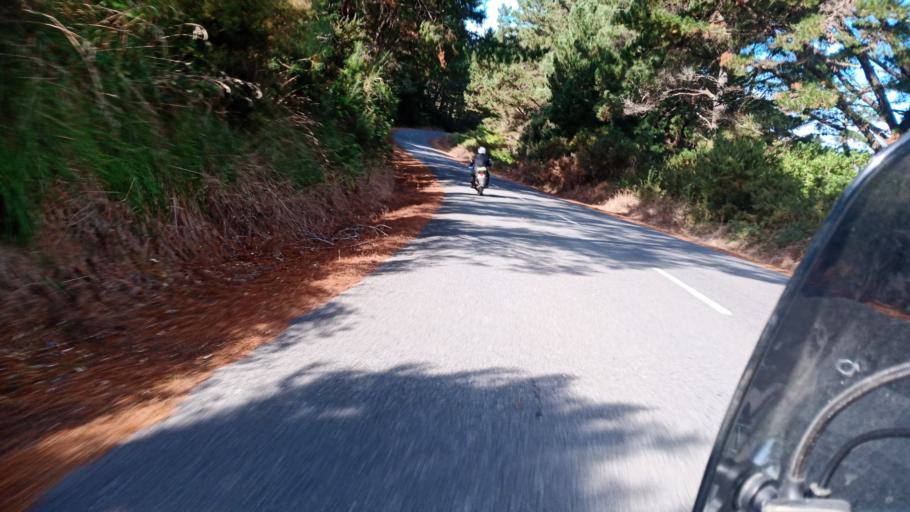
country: NZ
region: Hawke's Bay
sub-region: Wairoa District
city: Wairoa
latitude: -39.0447
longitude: 177.1138
